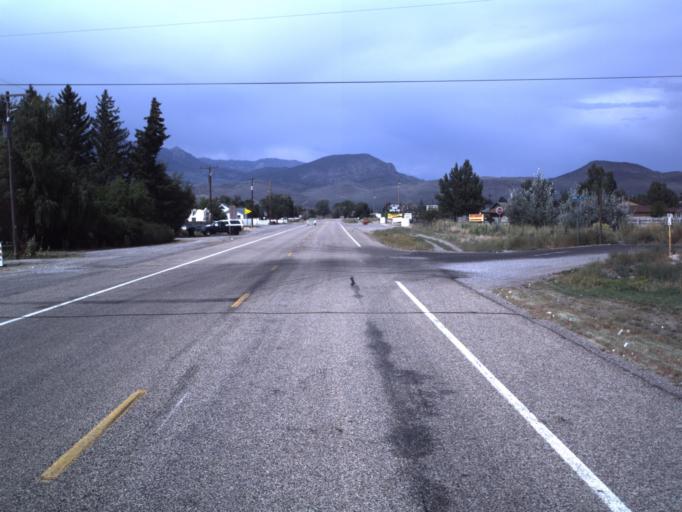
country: US
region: Utah
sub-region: Piute County
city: Junction
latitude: 38.1640
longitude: -112.2795
